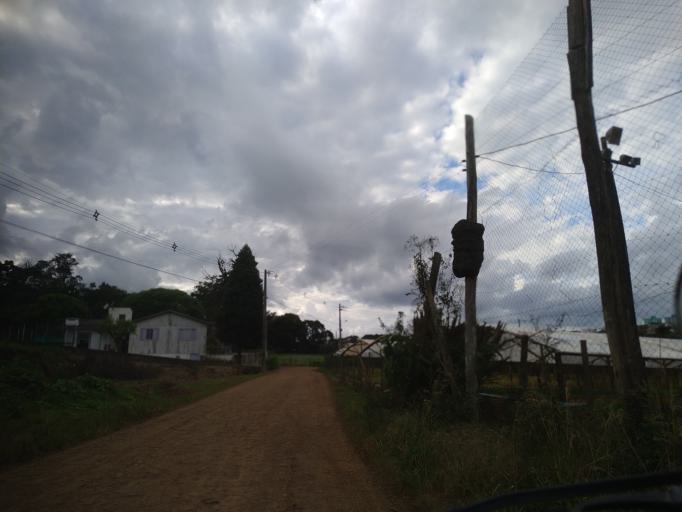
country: BR
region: Santa Catarina
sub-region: Chapeco
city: Chapeco
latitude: -27.0639
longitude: -52.6132
